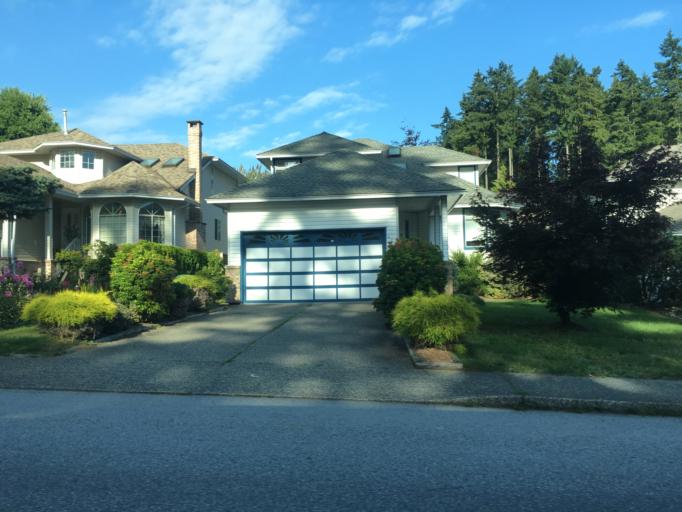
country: CA
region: British Columbia
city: Port Moody
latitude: 49.2464
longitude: -122.8244
